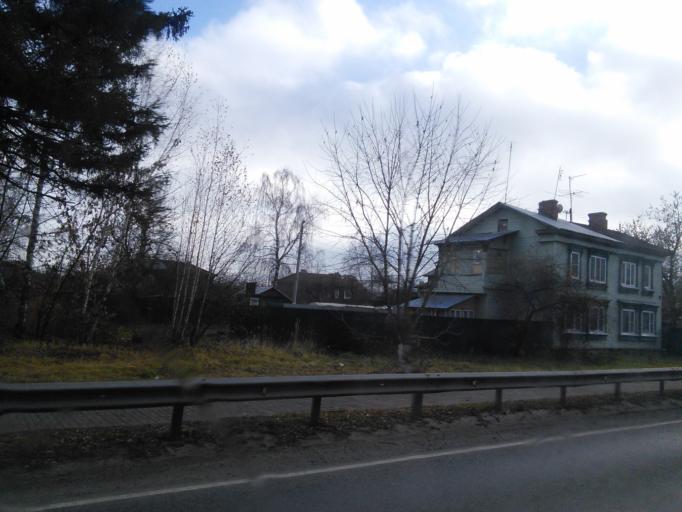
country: RU
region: Moskovskaya
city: Likino-Dulevo
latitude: 55.7100
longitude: 38.9578
